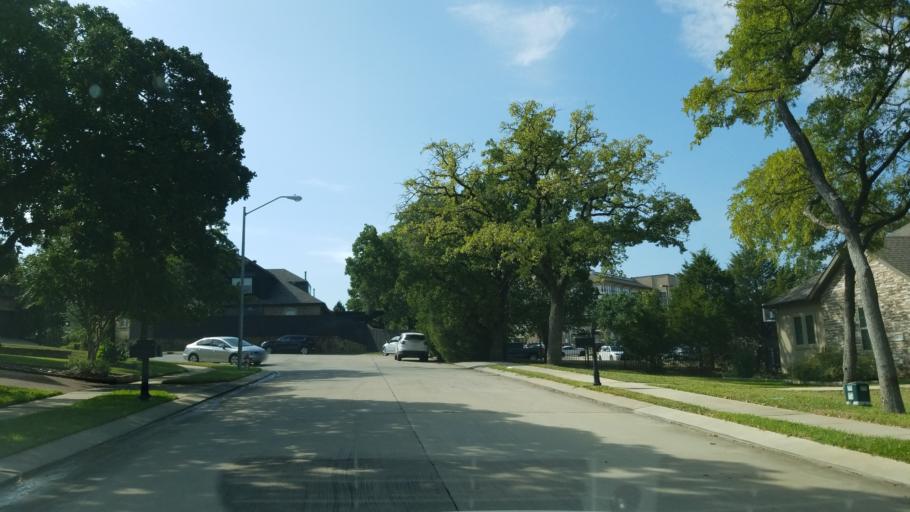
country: US
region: Texas
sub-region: Tarrant County
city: Grapevine
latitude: 32.8916
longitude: -97.0938
